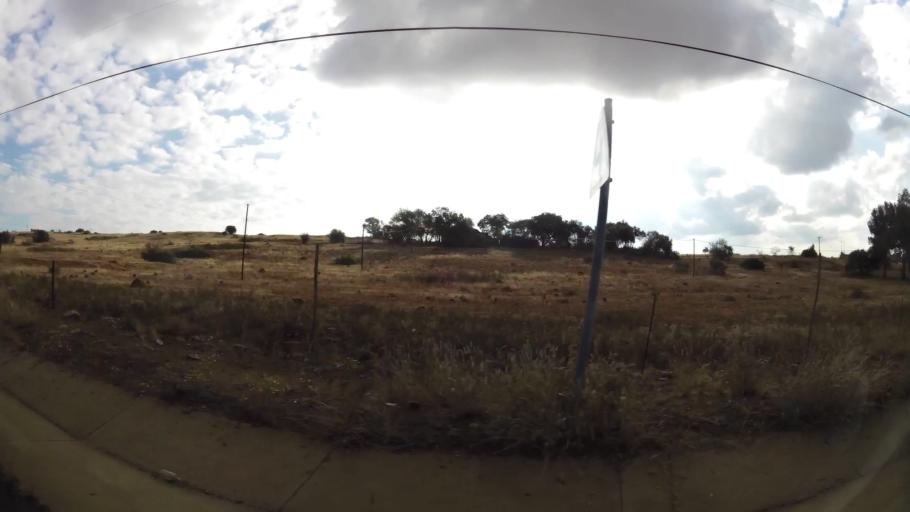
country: ZA
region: Orange Free State
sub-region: Mangaung Metropolitan Municipality
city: Bloemfontein
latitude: -29.0732
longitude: 26.1935
